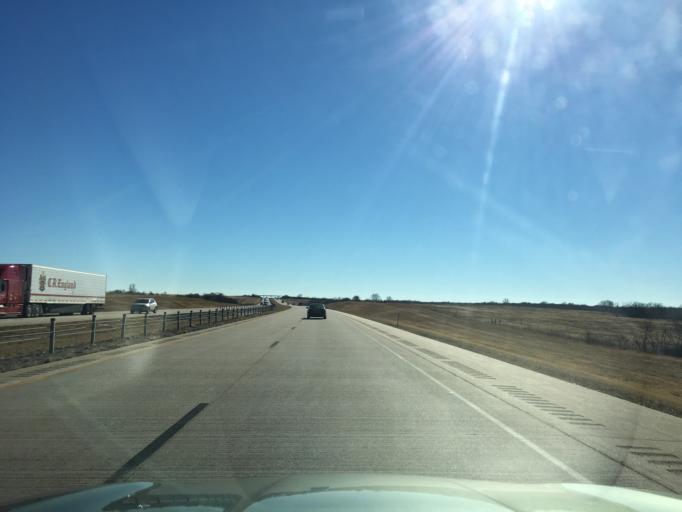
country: US
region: Oklahoma
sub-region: Kay County
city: Tonkawa
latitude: 36.5038
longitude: -97.3357
